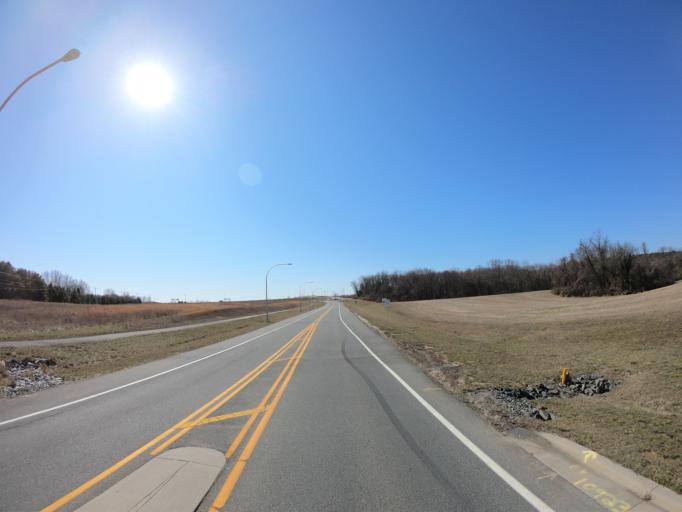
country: US
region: Delaware
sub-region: New Castle County
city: Middletown
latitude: 39.5298
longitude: -75.6785
